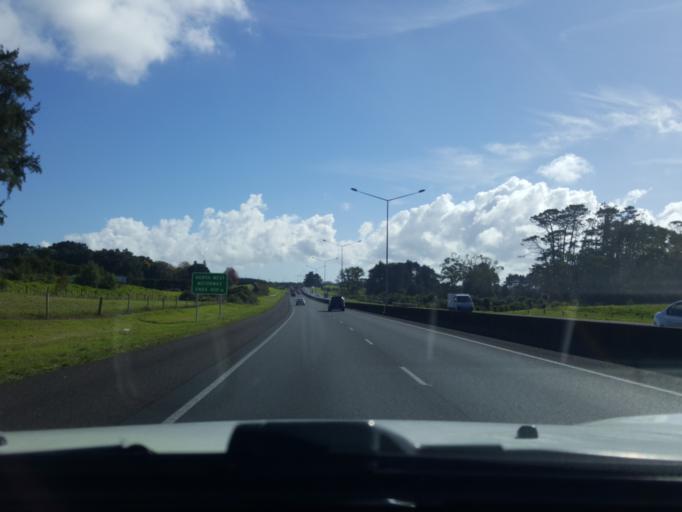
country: NZ
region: Auckland
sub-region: Auckland
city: Rosebank
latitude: -36.8024
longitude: 174.6028
